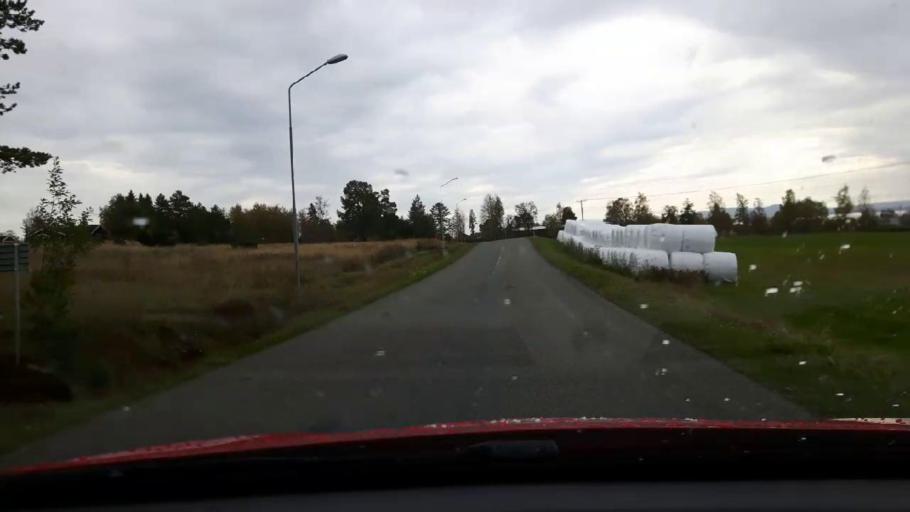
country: SE
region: Jaemtland
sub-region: Bergs Kommun
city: Hoverberg
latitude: 62.9501
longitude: 14.4910
